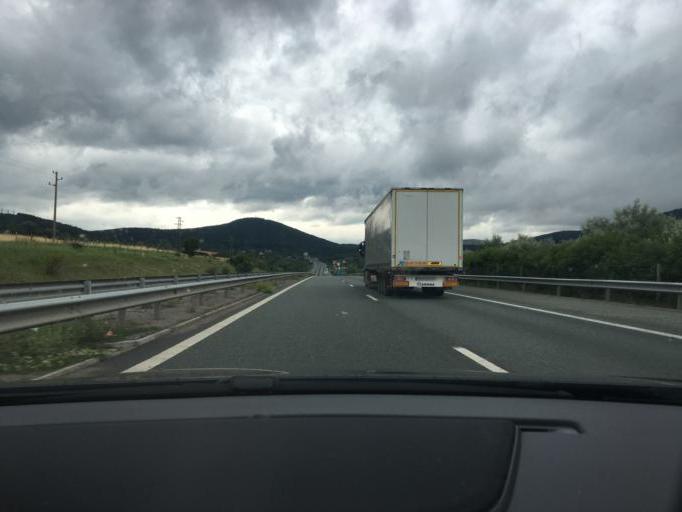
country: BG
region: Pernik
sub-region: Obshtina Pernik
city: Pernik
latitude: 42.5478
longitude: 23.1262
